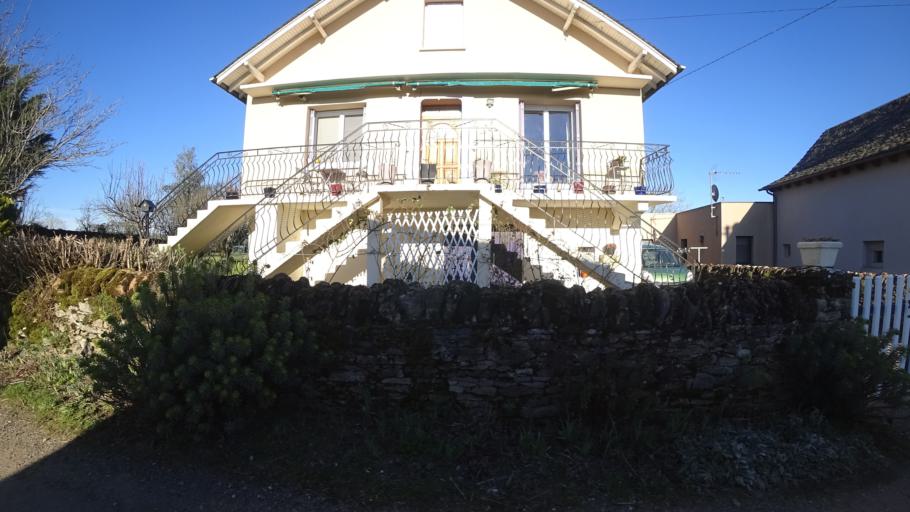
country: FR
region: Midi-Pyrenees
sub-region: Departement de l'Aveyron
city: Sebazac-Concoures
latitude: 44.4035
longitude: 2.5649
